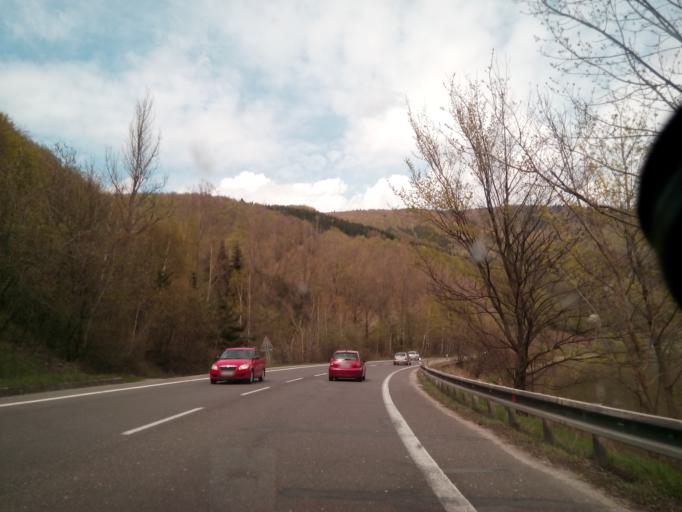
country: SK
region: Zilinsky
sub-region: Okres Zilina
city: Terchova
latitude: 49.1504
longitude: 19.1066
